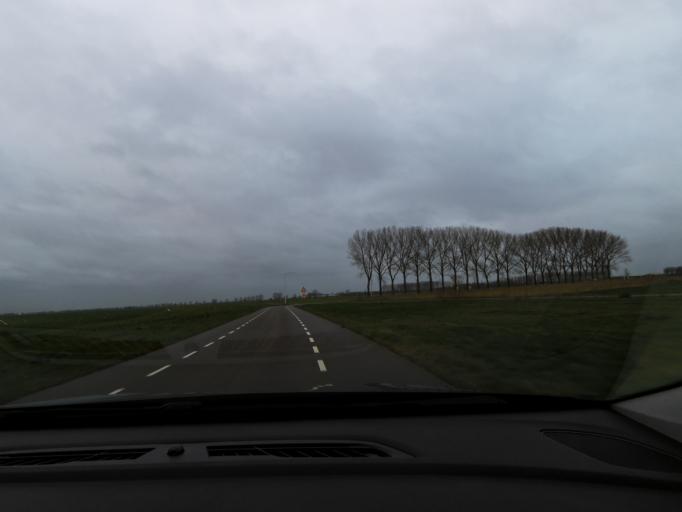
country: NL
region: North Brabant
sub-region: Gemeente Waalwijk
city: Waspik
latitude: 51.7149
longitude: 4.9811
